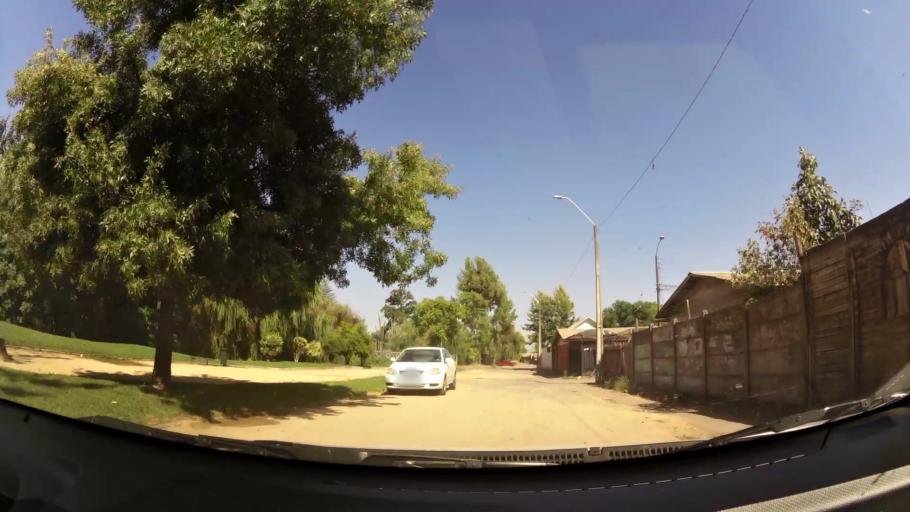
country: CL
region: Maule
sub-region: Provincia de Talca
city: Talca
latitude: -35.4331
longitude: -71.6678
